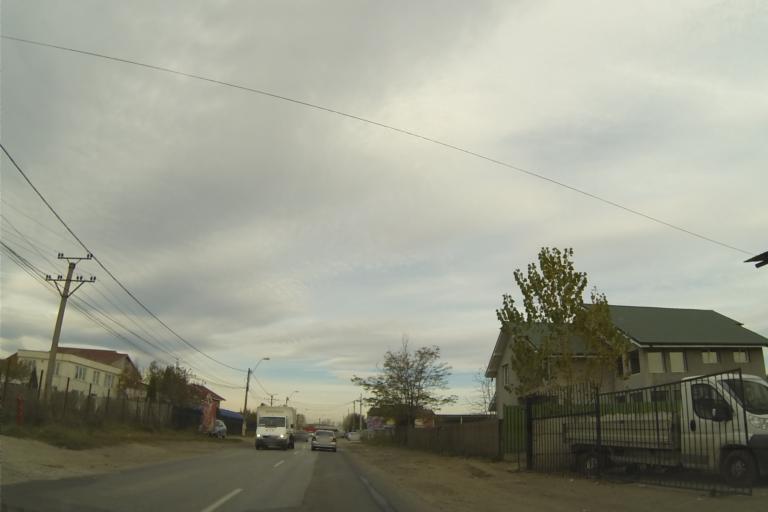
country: RO
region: Olt
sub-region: Municipiul Slatina
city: Slatina
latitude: 44.4366
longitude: 24.3647
